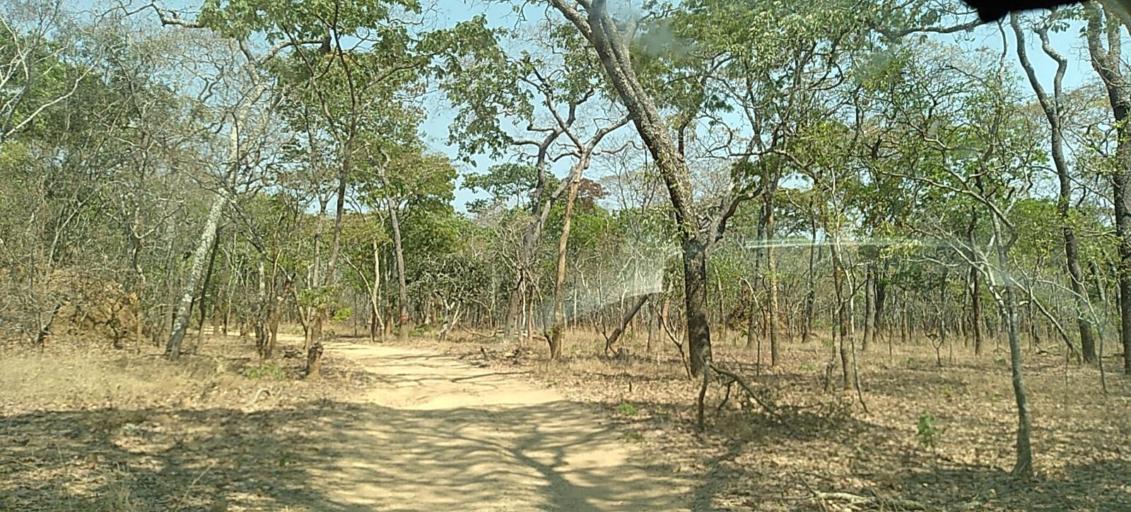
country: ZM
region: North-Western
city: Kasempa
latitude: -13.3926
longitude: 25.6235
